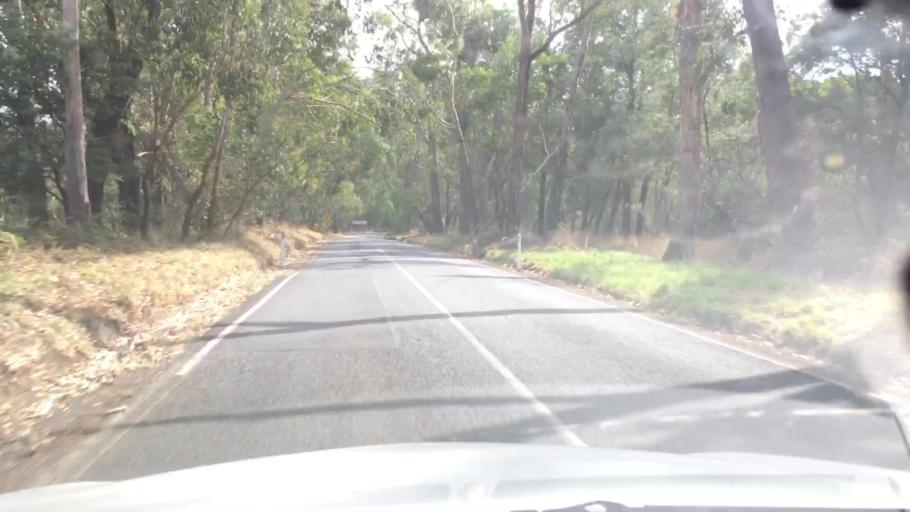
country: AU
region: Victoria
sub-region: Yarra Ranges
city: Woori Yallock
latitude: -37.8162
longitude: 145.4990
